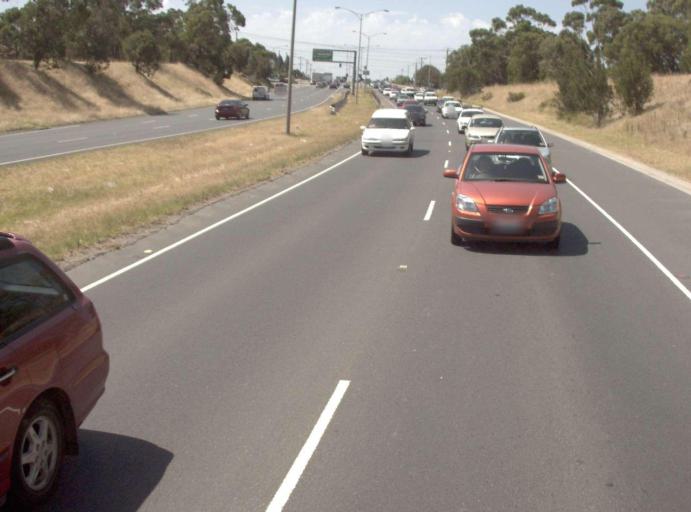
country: AU
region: Victoria
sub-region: Greater Dandenong
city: Springvale South
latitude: -37.9627
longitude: 145.1363
